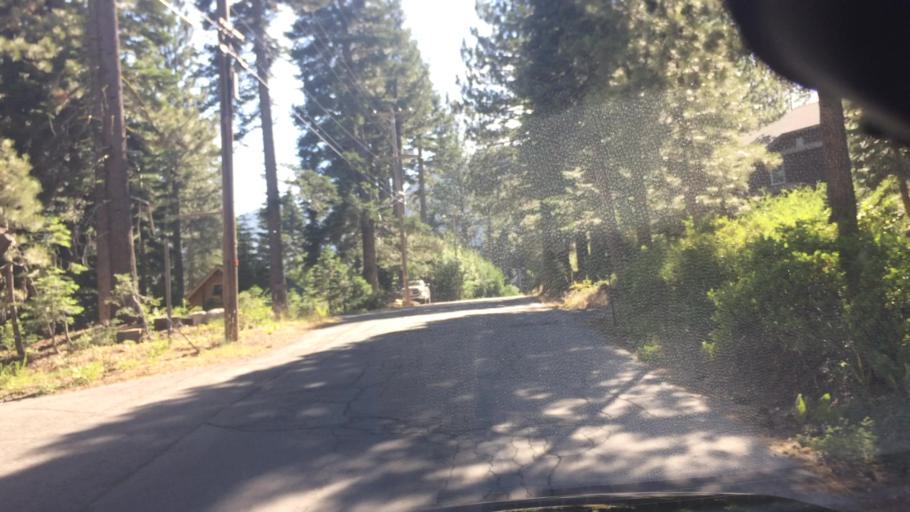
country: US
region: California
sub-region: Placer County
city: Sunnyside-Tahoe City
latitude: 39.2013
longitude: -120.2316
